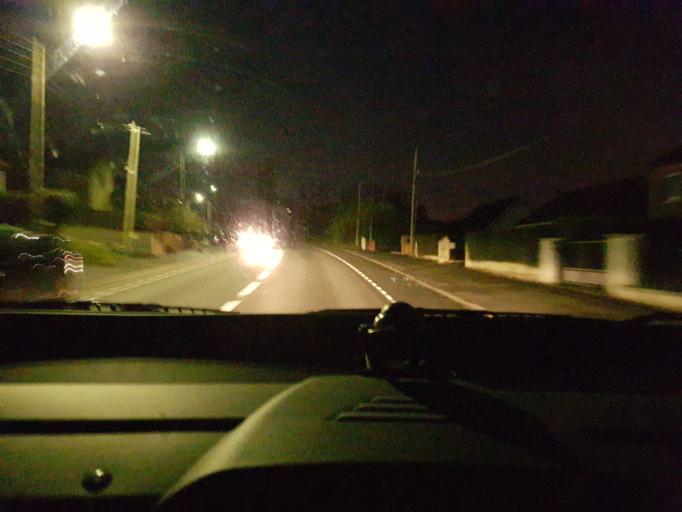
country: FR
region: Nord-Pas-de-Calais
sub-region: Departement du Pas-de-Calais
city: Souchez
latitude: 50.3973
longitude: 2.7424
